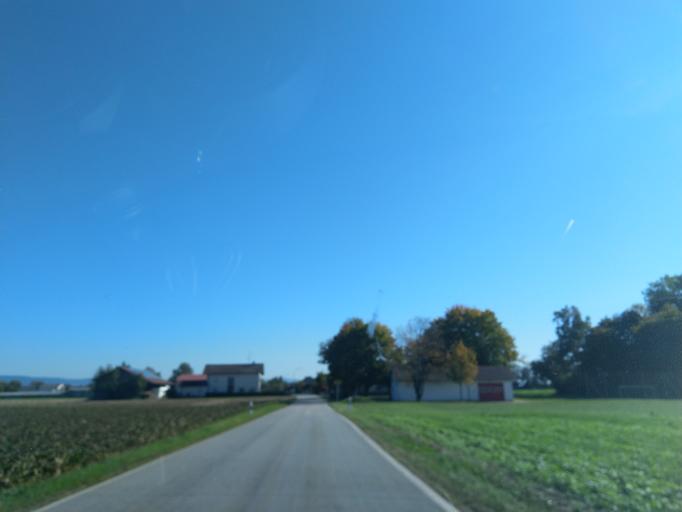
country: DE
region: Bavaria
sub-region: Lower Bavaria
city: Stephansposching
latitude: 48.7942
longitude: 12.7971
